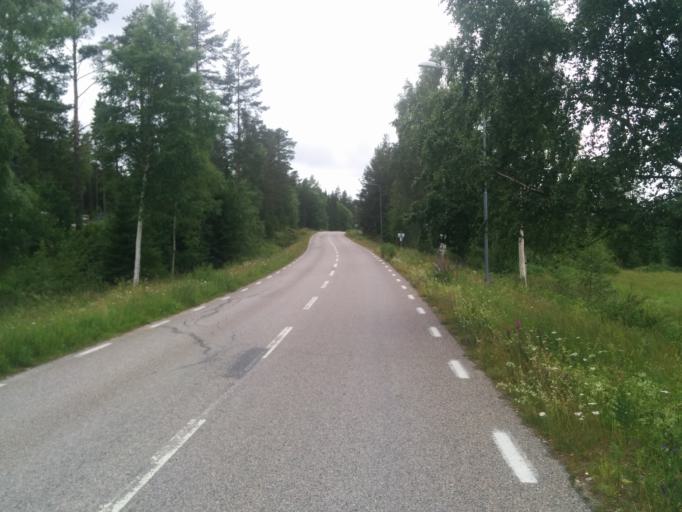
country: SE
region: Gaevleborg
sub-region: Nordanstigs Kommun
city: Bergsjoe
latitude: 61.9603
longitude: 17.3257
